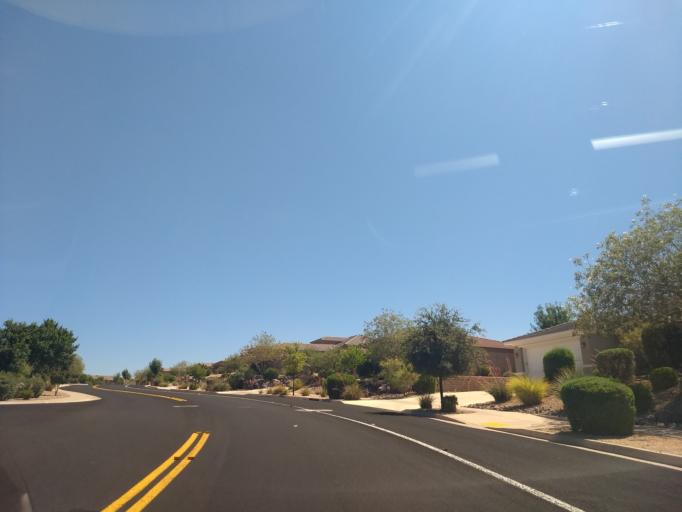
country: US
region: Utah
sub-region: Washington County
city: Washington
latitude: 37.1400
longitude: -113.4673
